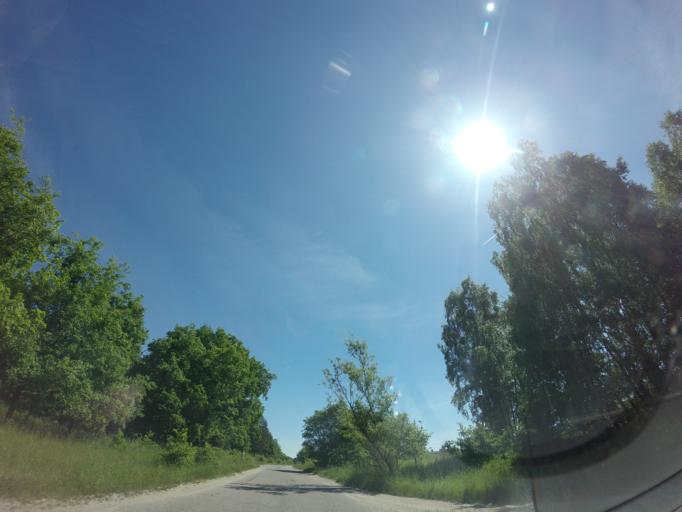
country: PL
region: West Pomeranian Voivodeship
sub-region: Powiat choszczenski
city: Recz
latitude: 53.3098
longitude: 15.6363
